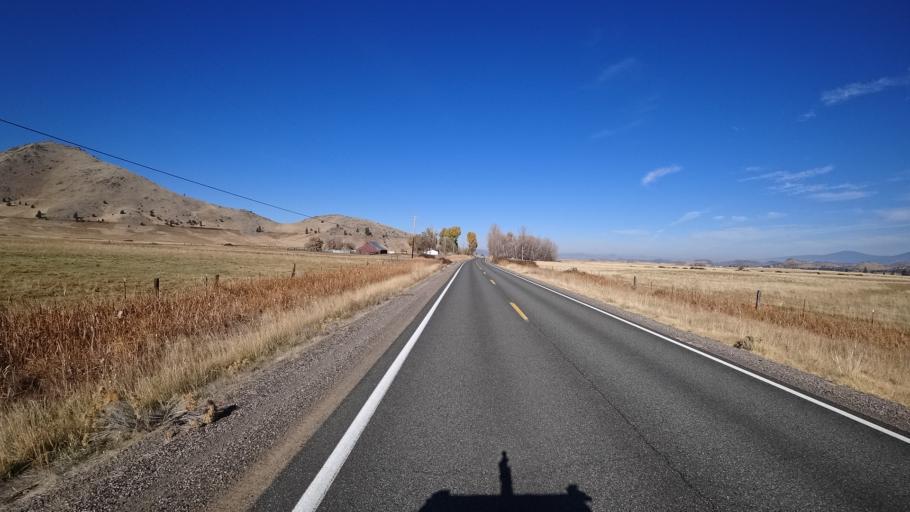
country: US
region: California
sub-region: Siskiyou County
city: Weed
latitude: 41.4566
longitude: -122.4604
